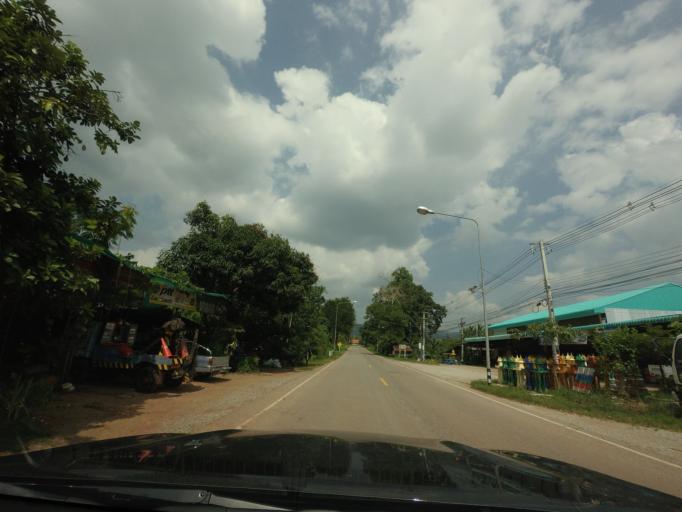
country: TH
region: Uttaradit
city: Ban Khok
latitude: 18.0390
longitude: 101.1009
